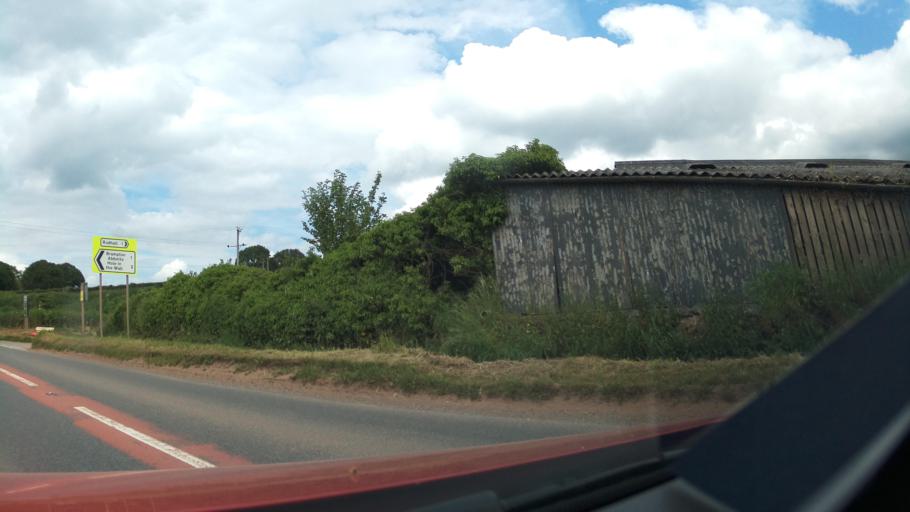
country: GB
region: England
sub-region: Herefordshire
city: Ross on Wye
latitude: 51.9347
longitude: -2.5597
